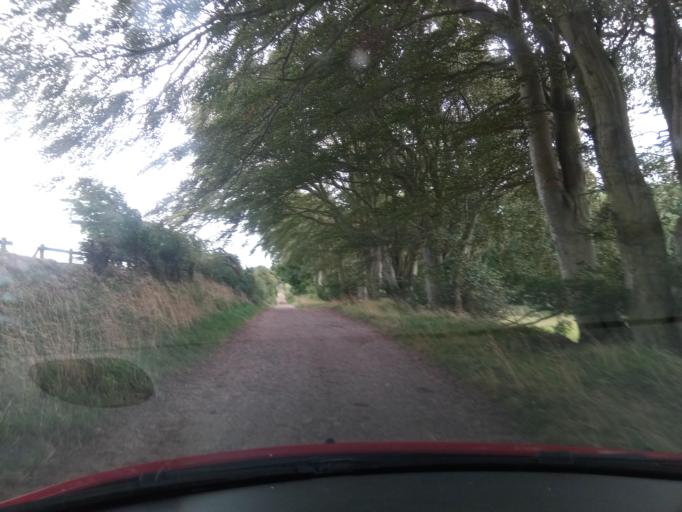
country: GB
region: Scotland
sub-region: The Scottish Borders
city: Jedburgh
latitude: 55.4887
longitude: -2.5228
